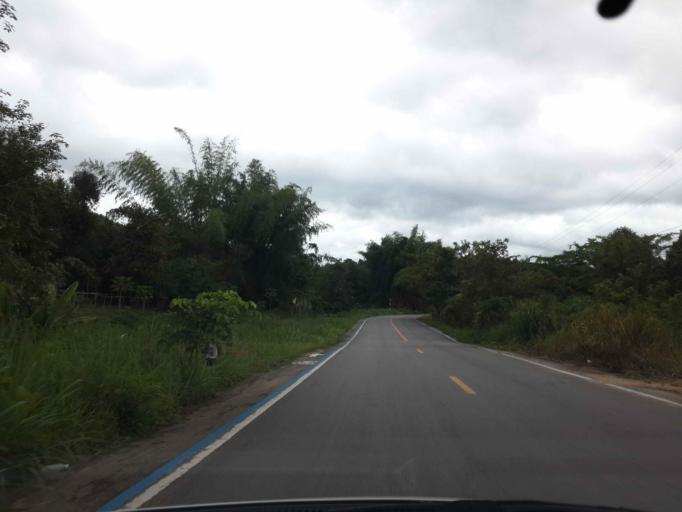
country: TH
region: Ratchaburi
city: Suan Phueng
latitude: 13.6053
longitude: 99.2300
